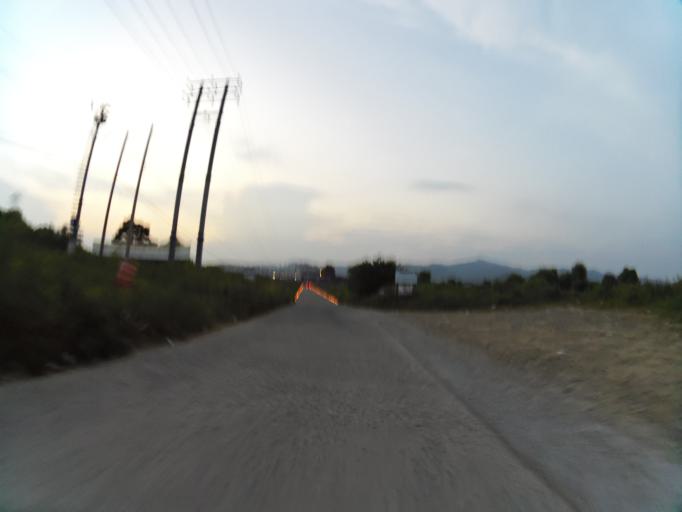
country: KR
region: Gyeongsangbuk-do
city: Gyeongsan-si
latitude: 35.8565
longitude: 128.7400
